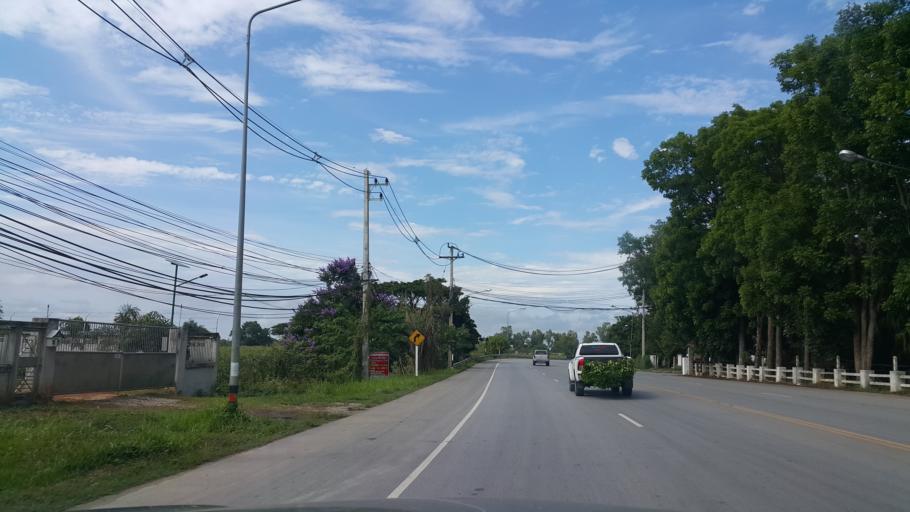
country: TH
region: Chiang Rai
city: Chiang Rai
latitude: 19.9103
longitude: 99.8614
